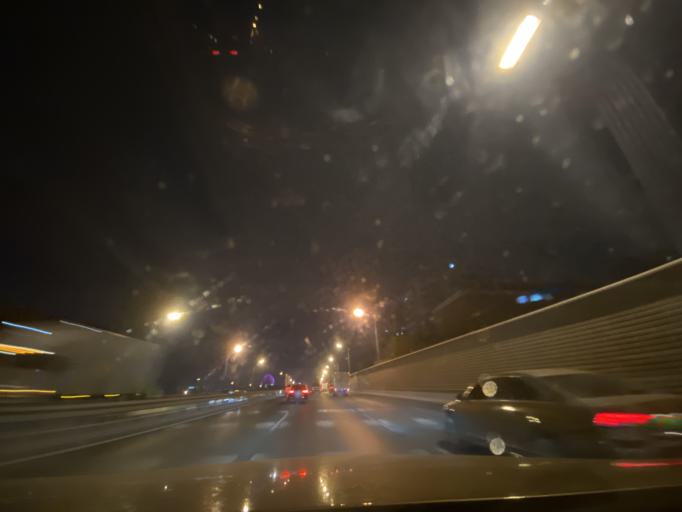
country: CN
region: Beijing
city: Lugu
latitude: 39.9038
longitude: 116.2051
